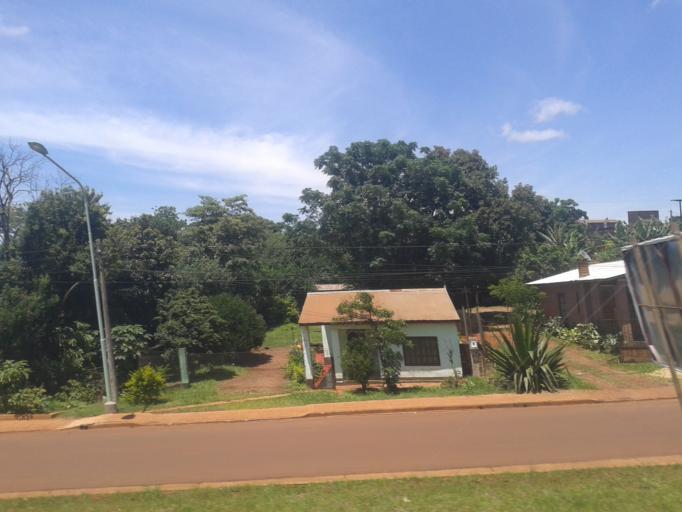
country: AR
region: Misiones
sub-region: Departamento de Leandro N. Alem
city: Leandro N. Alem
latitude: -27.6042
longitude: -55.3393
